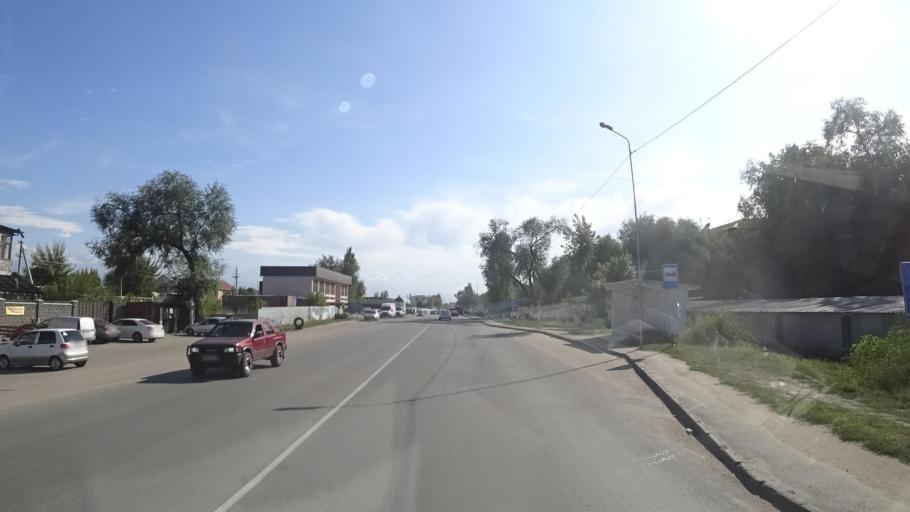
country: KZ
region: Almaty Oblysy
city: Energeticheskiy
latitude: 43.4217
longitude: 77.0232
